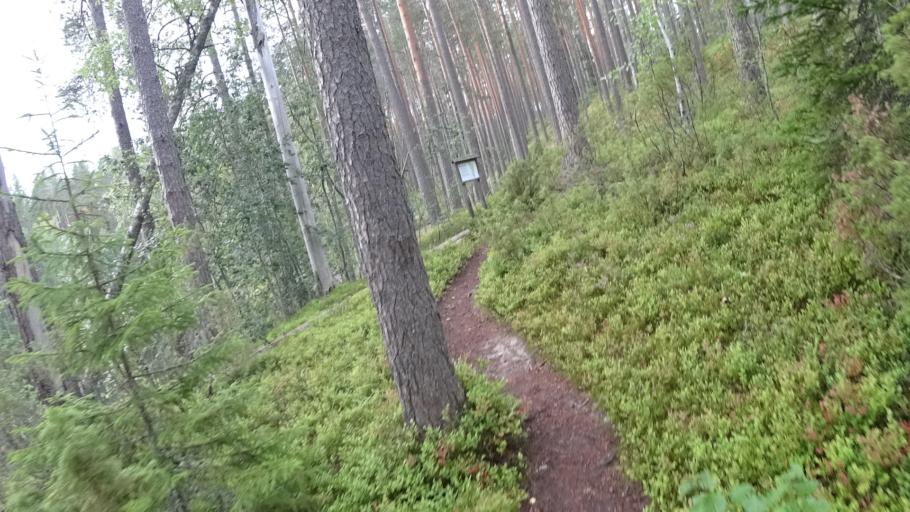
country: FI
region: North Karelia
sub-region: Joensuu
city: Ilomantsi
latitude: 62.5810
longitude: 31.1710
